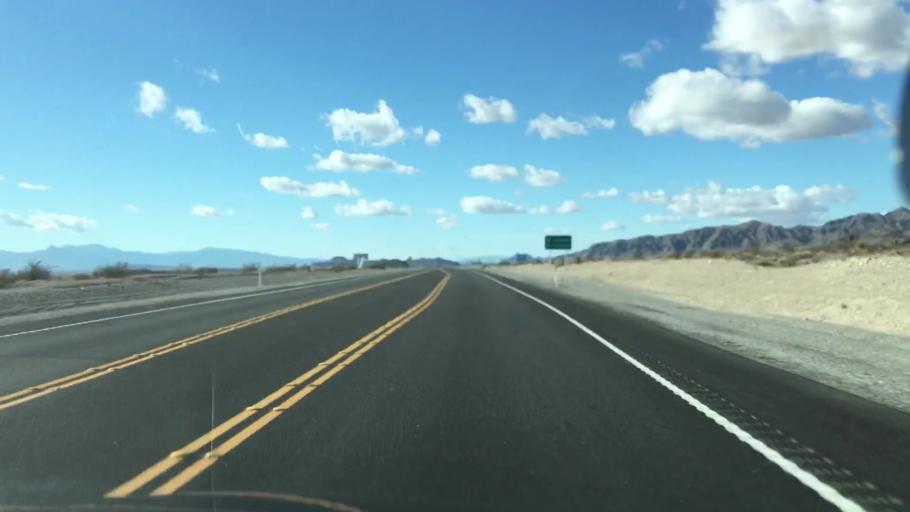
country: US
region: Nevada
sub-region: Nye County
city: Pahrump
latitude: 36.5643
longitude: -116.1195
